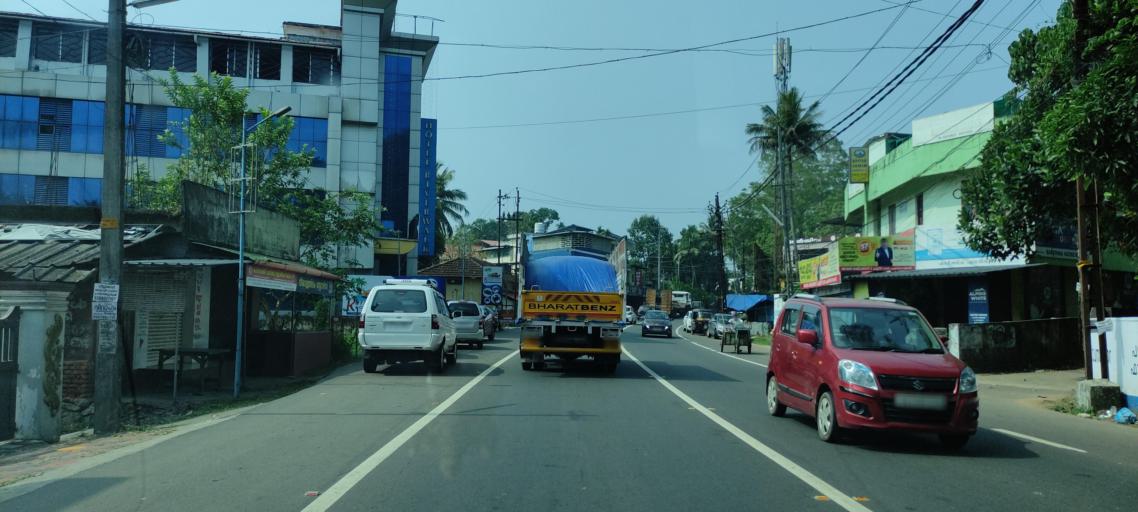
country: IN
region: Kerala
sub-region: Pattanamtitta
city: Adur
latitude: 9.2314
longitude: 76.6756
